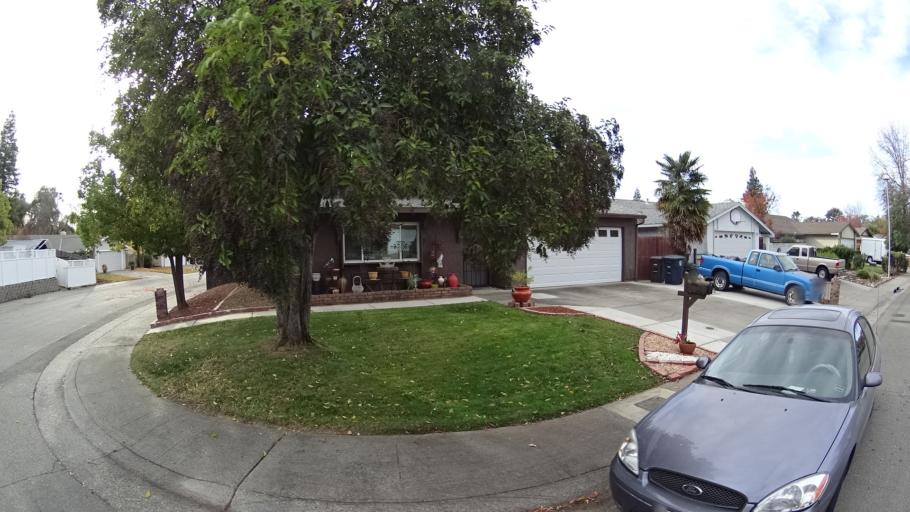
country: US
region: California
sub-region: Sacramento County
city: Citrus Heights
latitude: 38.7069
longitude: -121.2581
